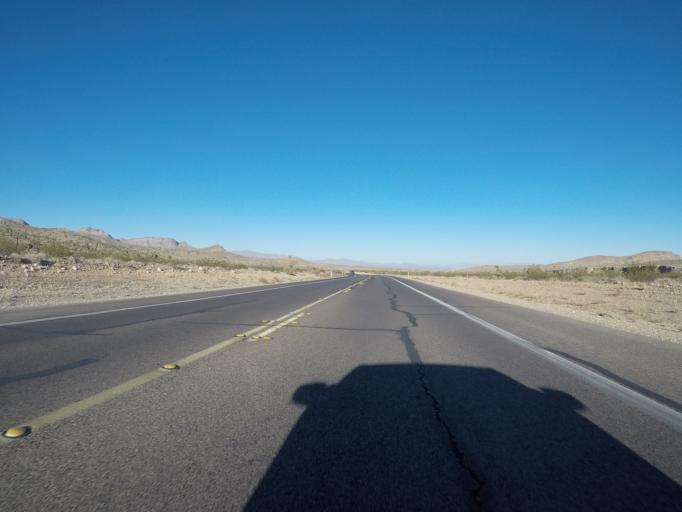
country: US
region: Nevada
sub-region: Clark County
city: Summerlin South
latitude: 36.1347
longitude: -115.4109
